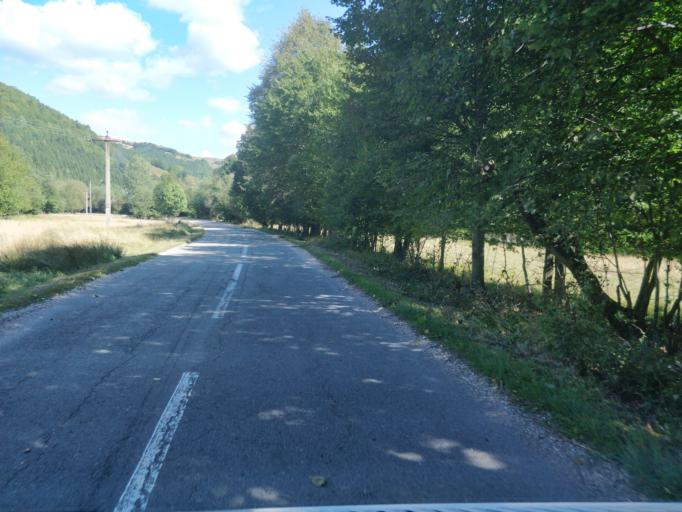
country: RO
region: Cluj
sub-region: Comuna Sacueu
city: Sacuieu
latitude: 46.8478
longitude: 22.8628
